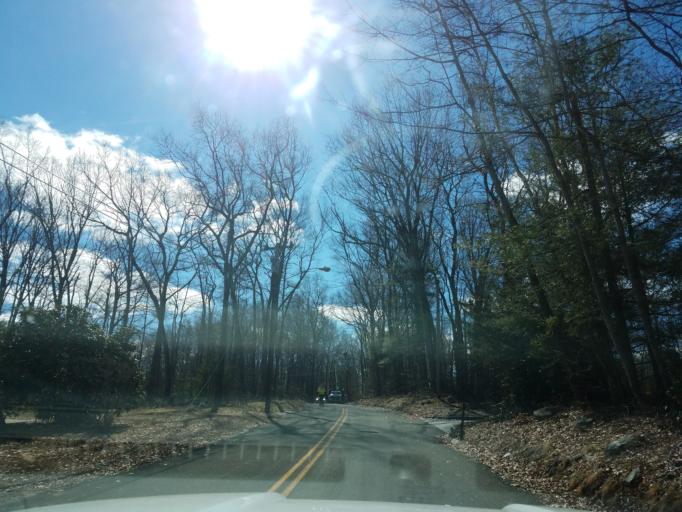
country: US
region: Connecticut
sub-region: Windham County
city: North Grosvenor Dale
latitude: 41.9993
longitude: -71.8815
